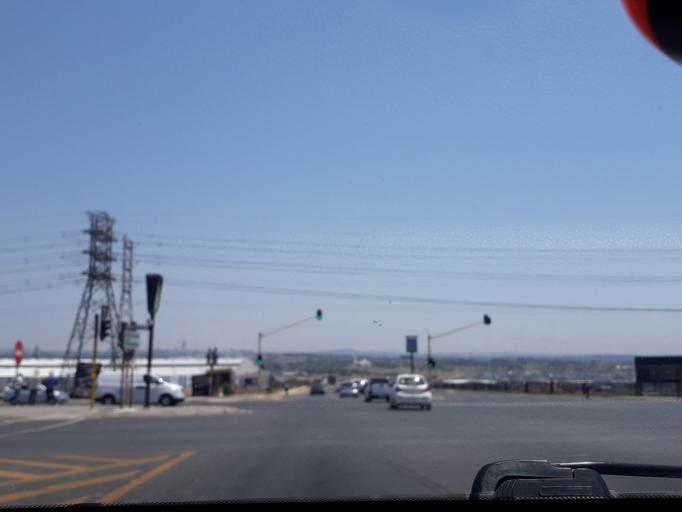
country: ZA
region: Gauteng
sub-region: City of Johannesburg Metropolitan Municipality
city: Midrand
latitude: -26.0189
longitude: 28.1230
